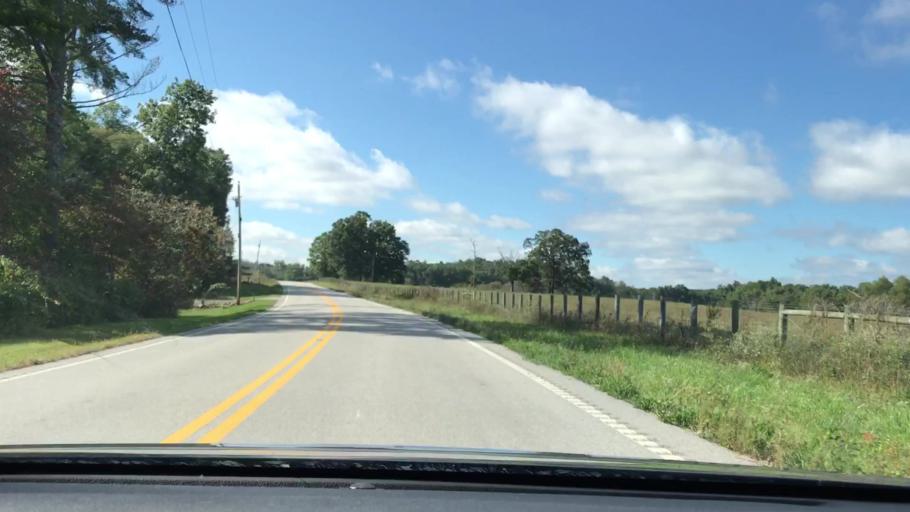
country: US
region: Tennessee
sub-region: Fentress County
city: Jamestown
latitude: 36.3627
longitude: -84.7451
